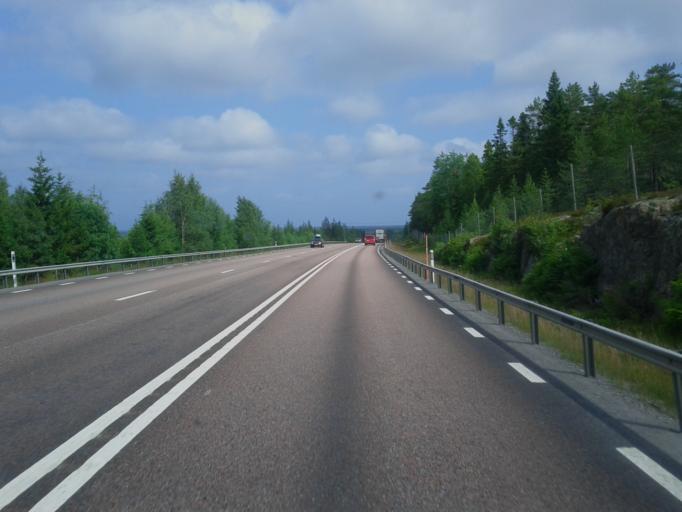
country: SE
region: Vaesterbotten
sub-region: Skelleftea Kommun
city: Burea
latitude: 64.4537
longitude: 21.2855
